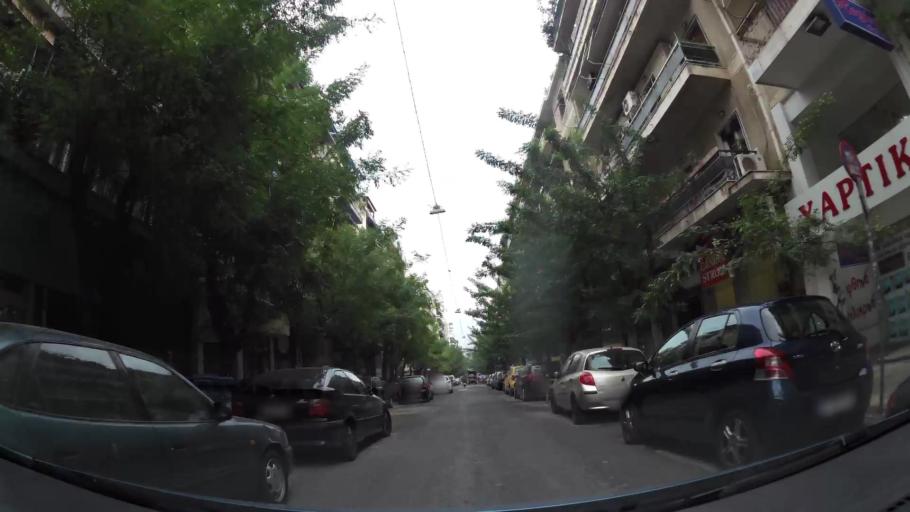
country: GR
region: Attica
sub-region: Nomarchia Athinas
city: Vyronas
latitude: 37.9702
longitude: 23.7518
